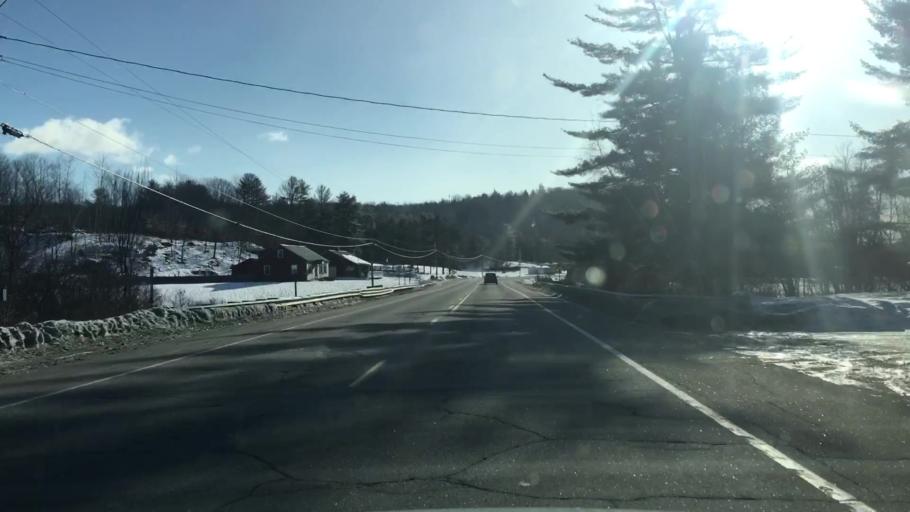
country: US
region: Maine
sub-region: Oxford County
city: West Paris
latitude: 44.3251
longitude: -70.5485
